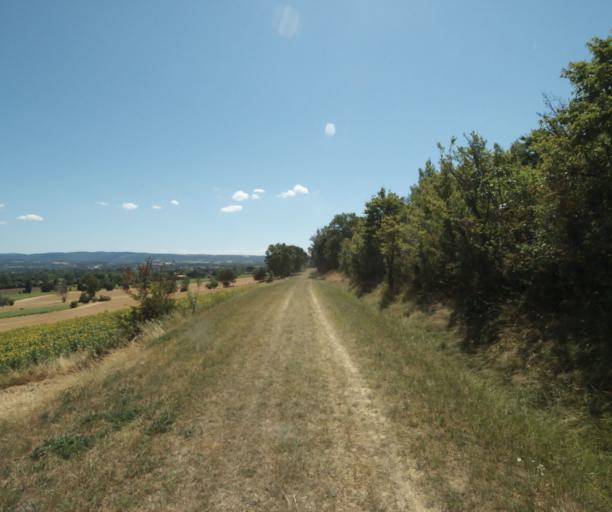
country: FR
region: Midi-Pyrenees
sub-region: Departement de la Haute-Garonne
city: Saint-Felix-Lauragais
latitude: 43.4691
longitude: 1.9209
